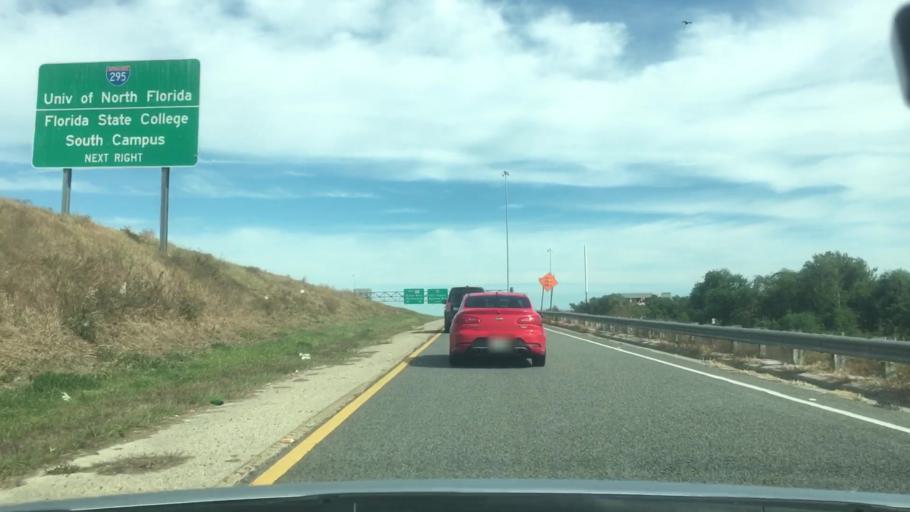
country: US
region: Florida
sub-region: Duval County
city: Jacksonville
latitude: 30.2499
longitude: -81.5340
